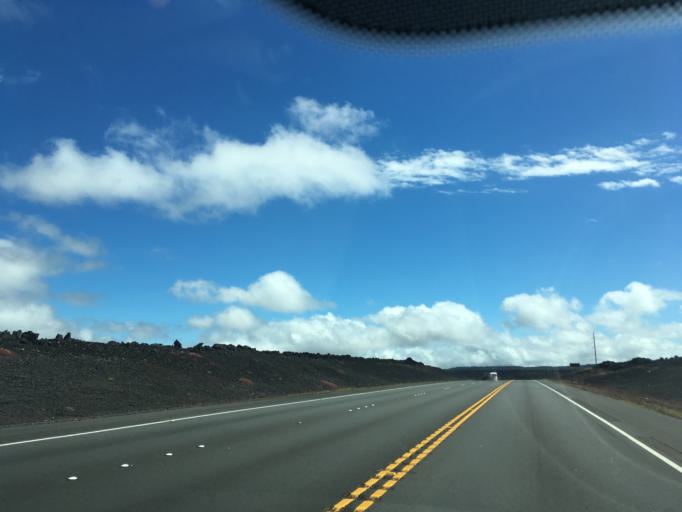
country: US
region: Hawaii
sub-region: Hawaii County
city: Volcano
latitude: 19.6802
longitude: -155.3904
